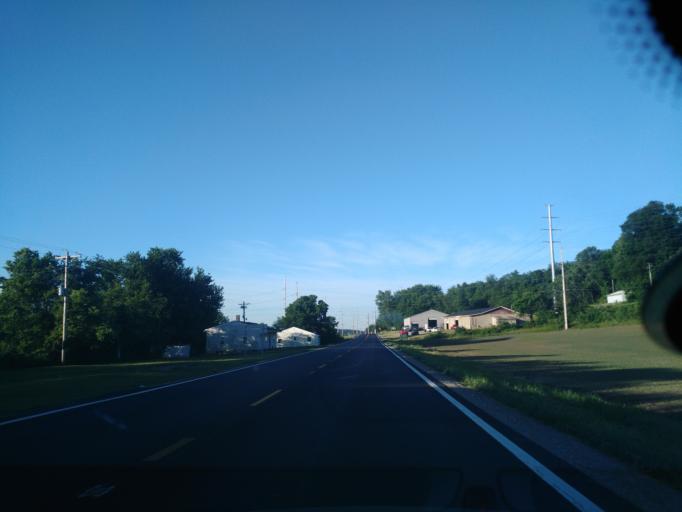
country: US
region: Ohio
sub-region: Ross County
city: Chillicothe
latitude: 39.4057
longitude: -82.9602
